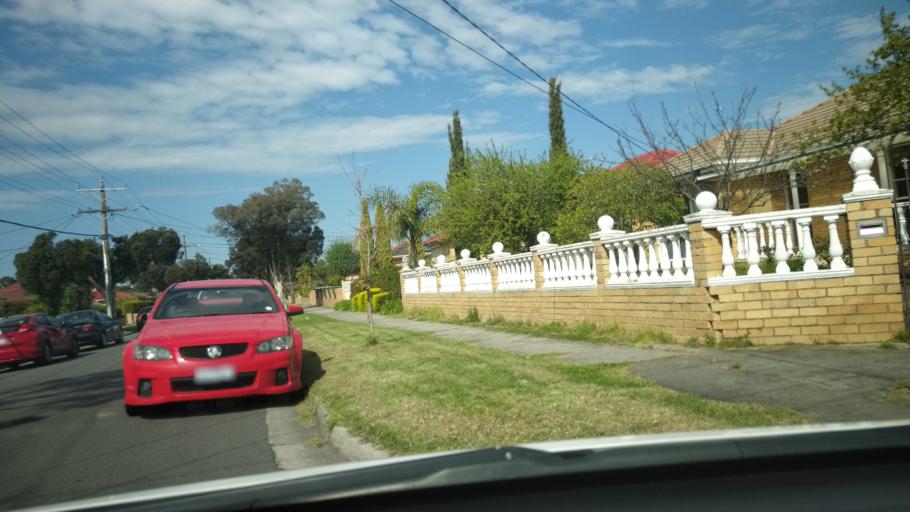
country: AU
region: Victoria
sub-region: Greater Dandenong
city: Noble Park
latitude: -37.9581
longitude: 145.1610
